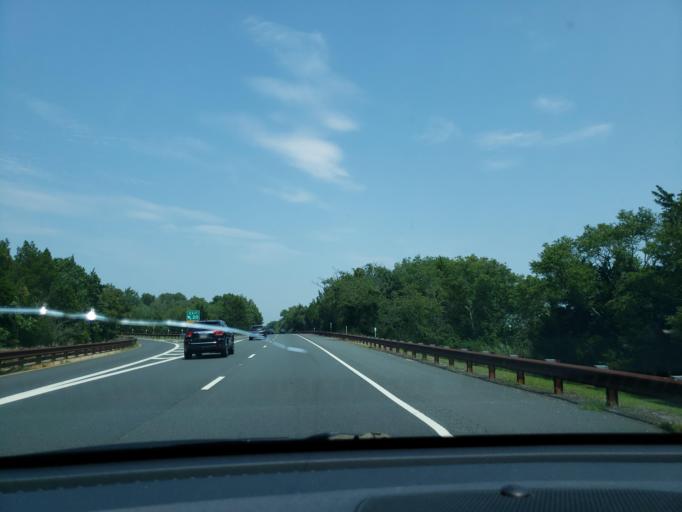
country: US
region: New Jersey
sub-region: Cape May County
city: Sea Isle City
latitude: 39.2020
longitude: -74.7001
